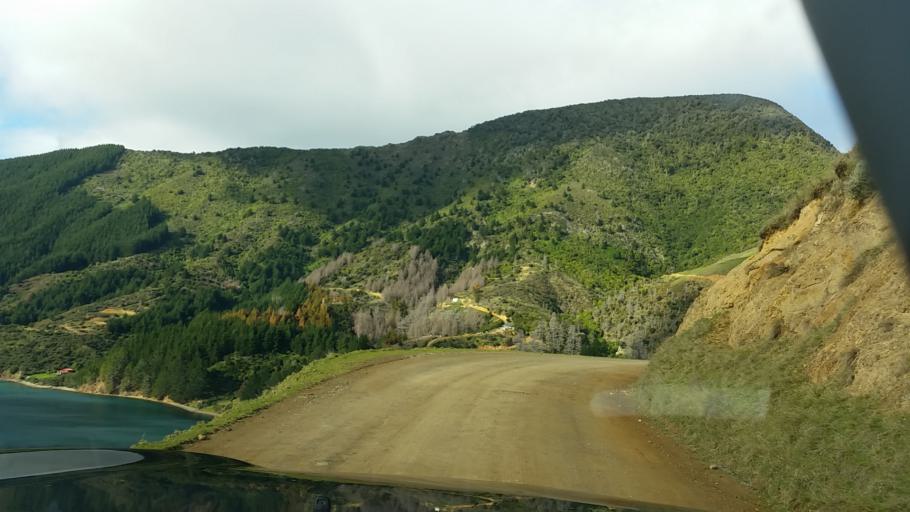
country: NZ
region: Marlborough
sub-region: Marlborough District
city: Picton
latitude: -40.9855
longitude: 173.8423
